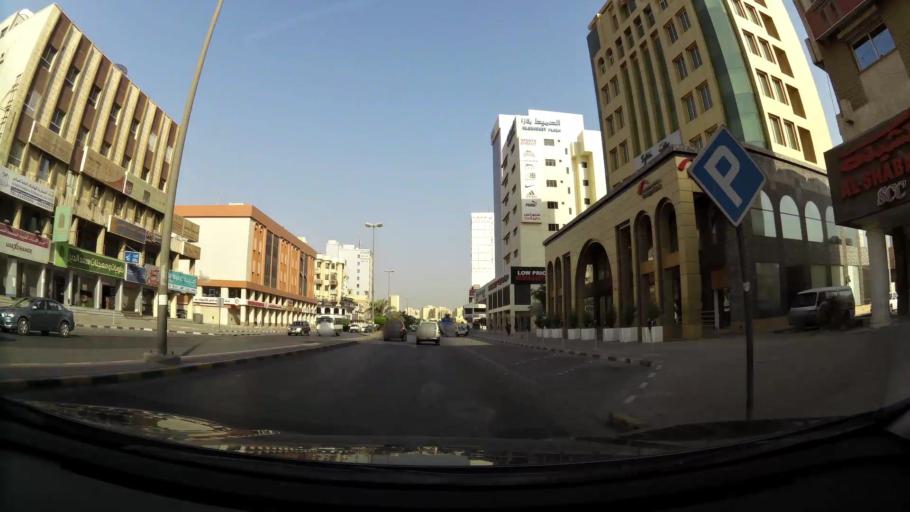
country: KW
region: Muhafazat Hawalli
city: Hawalli
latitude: 29.3341
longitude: 48.0262
